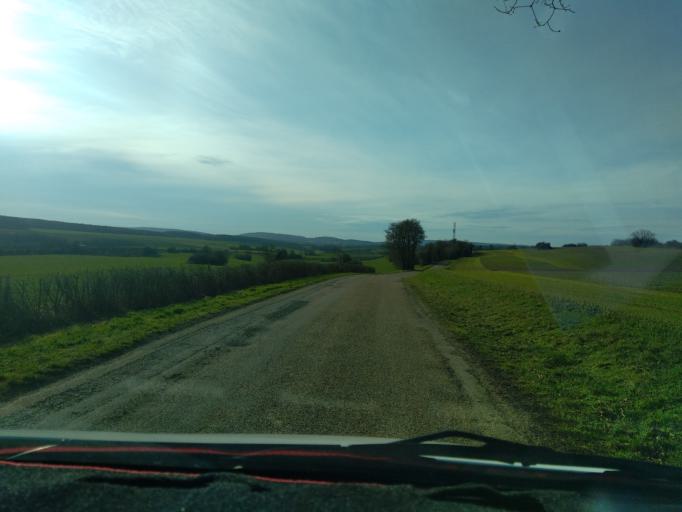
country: FR
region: Franche-Comte
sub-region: Departement de la Haute-Saone
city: Marnay
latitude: 47.3151
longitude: 5.6796
